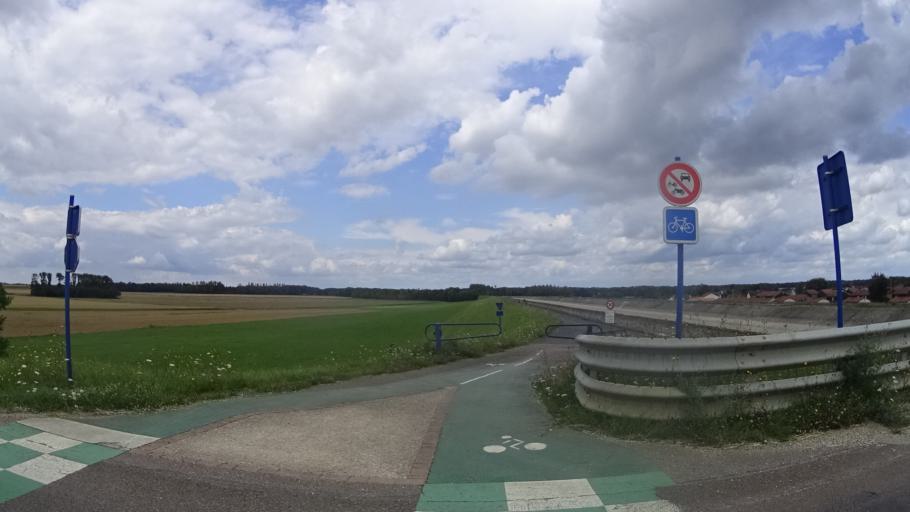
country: FR
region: Champagne-Ardenne
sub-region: Departement de la Haute-Marne
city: Villiers-en-Lieu
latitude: 48.5925
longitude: 4.8584
